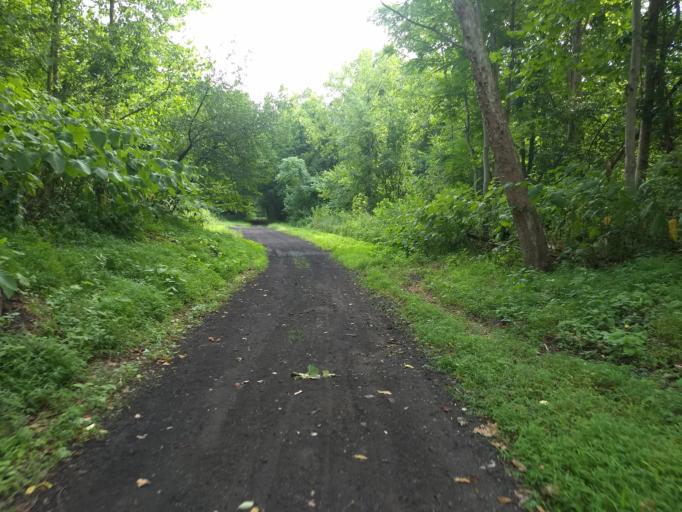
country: US
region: Pennsylvania
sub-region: Armstrong County
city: Freeport
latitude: 40.6757
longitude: -79.6681
